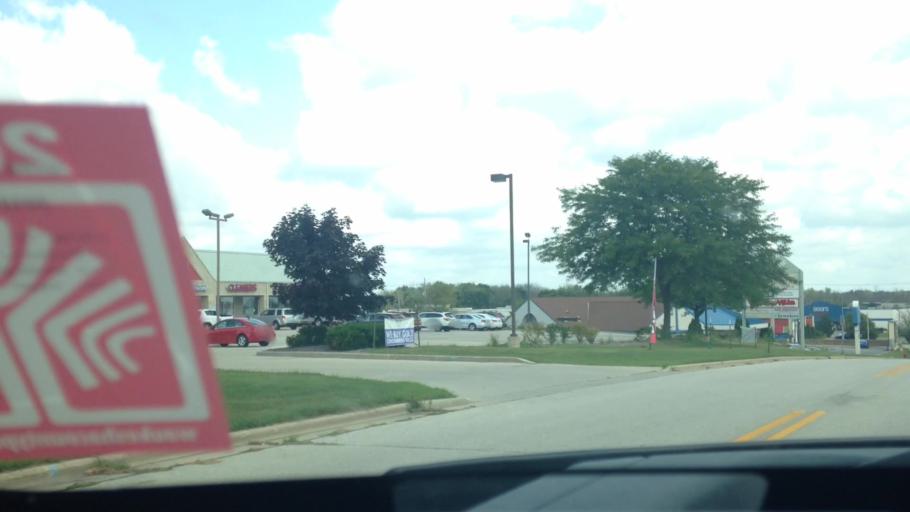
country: US
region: Wisconsin
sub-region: Waukesha County
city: Menomonee Falls
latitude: 43.1902
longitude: -88.1404
